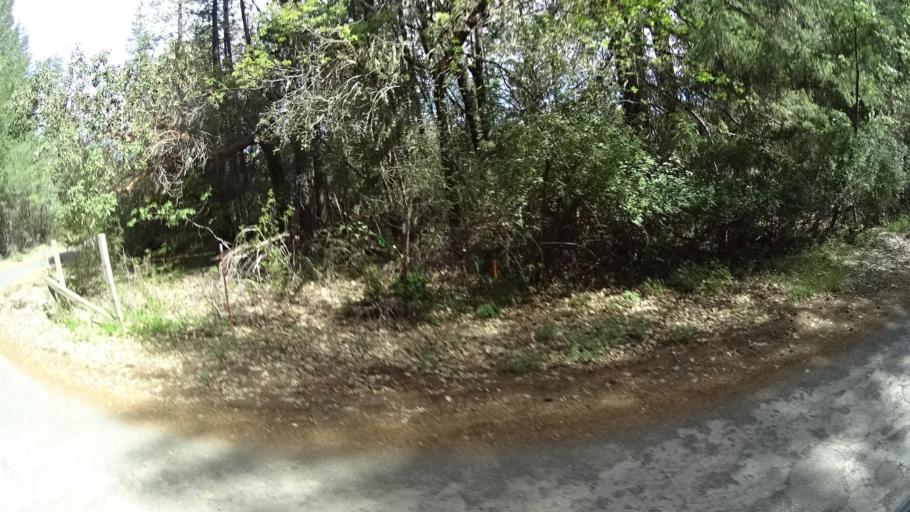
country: US
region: California
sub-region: Lake County
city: Cobb
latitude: 38.8829
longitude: -122.7786
